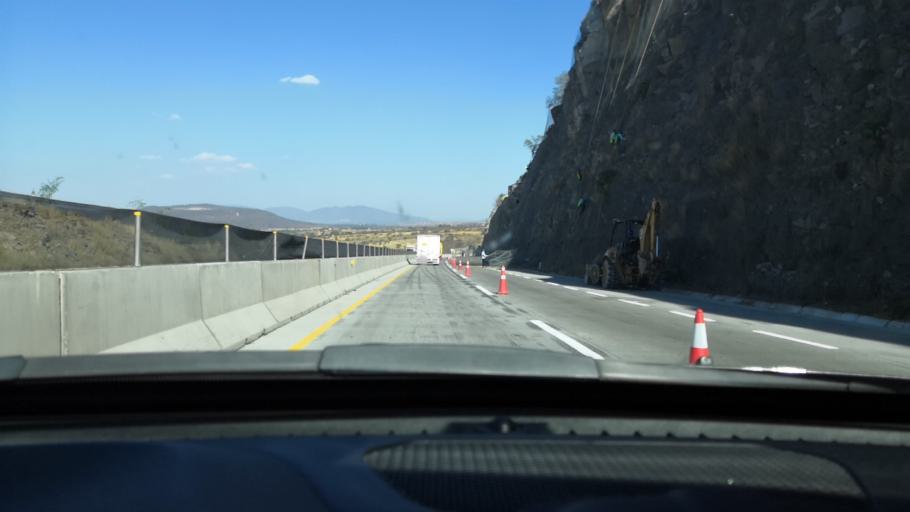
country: MX
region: Jalisco
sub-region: Tlajomulco de Zuniga
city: San Lucas Evangelista
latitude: 20.3916
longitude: -103.3345
